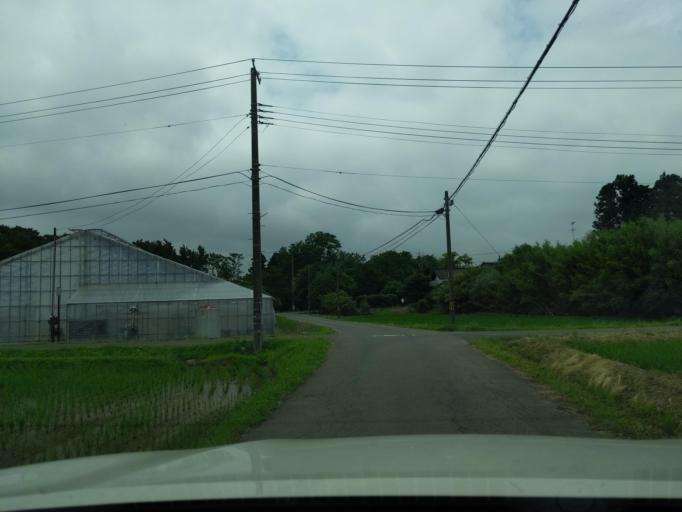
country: JP
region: Fukushima
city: Koriyama
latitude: 37.4199
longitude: 140.3286
